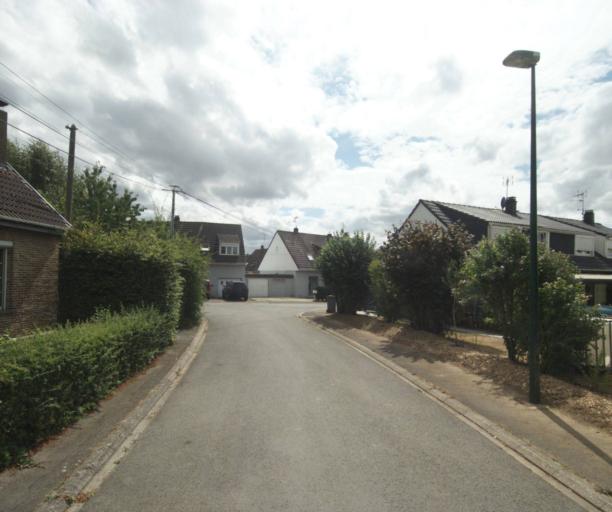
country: FR
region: Nord-Pas-de-Calais
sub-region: Departement du Nord
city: Roncq
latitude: 50.7554
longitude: 3.1140
